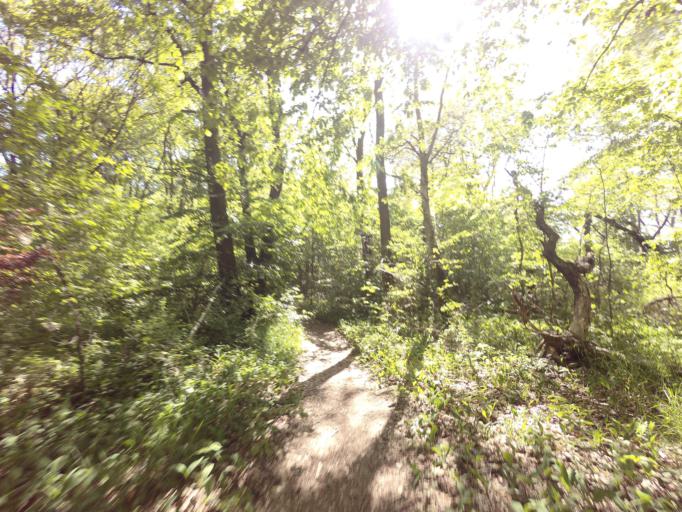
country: DE
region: Lower Saxony
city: Lehre
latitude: 52.2974
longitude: 10.6665
